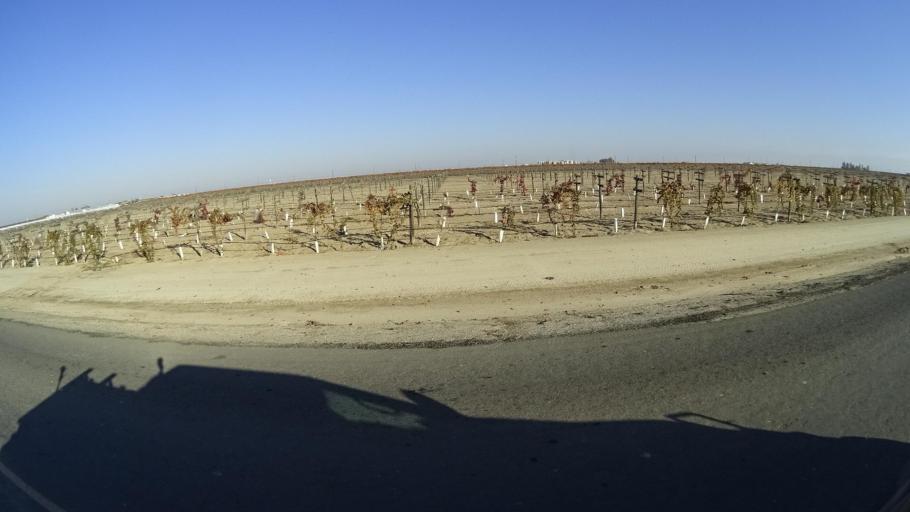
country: US
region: California
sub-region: Kern County
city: Delano
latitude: 35.7687
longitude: -119.1950
